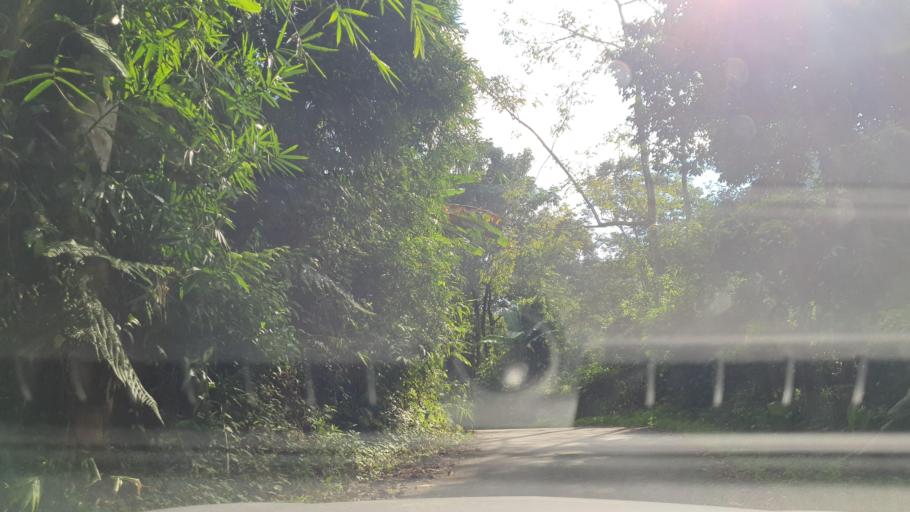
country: TH
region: Chiang Mai
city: Mae On
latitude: 18.9355
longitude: 99.3114
